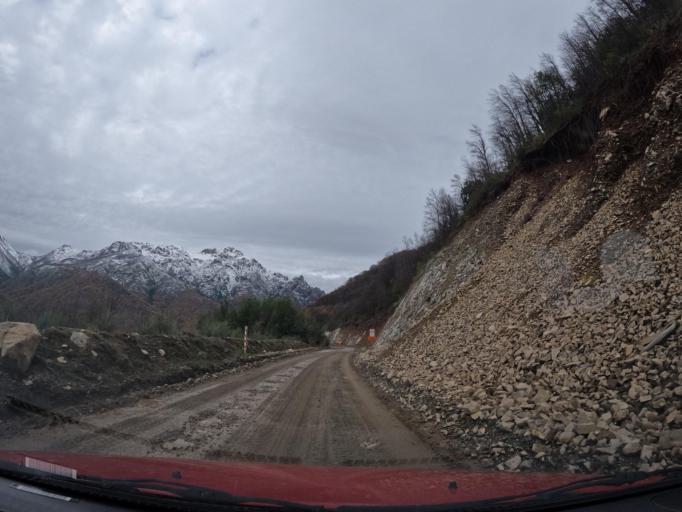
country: CL
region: Maule
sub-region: Provincia de Linares
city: Colbun
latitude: -35.8584
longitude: -71.1526
